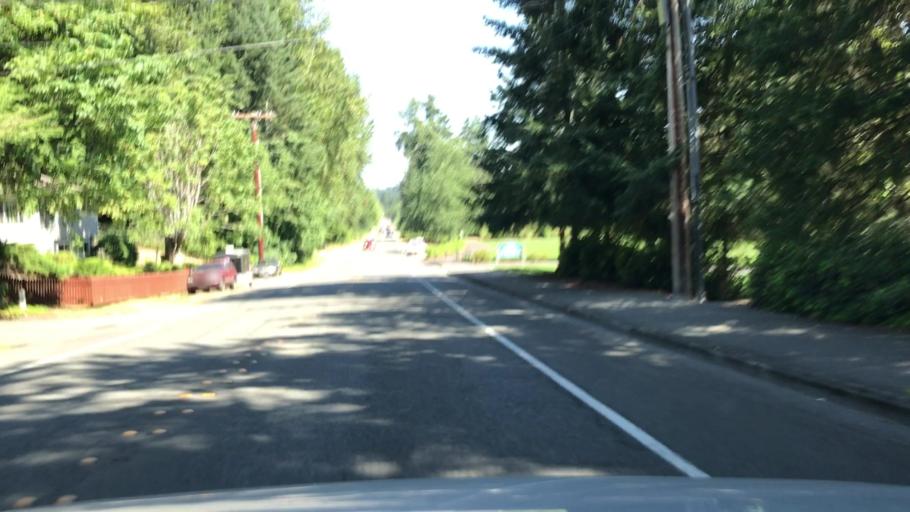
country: US
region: Washington
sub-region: King County
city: Eastgate
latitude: 47.5919
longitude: -122.1319
